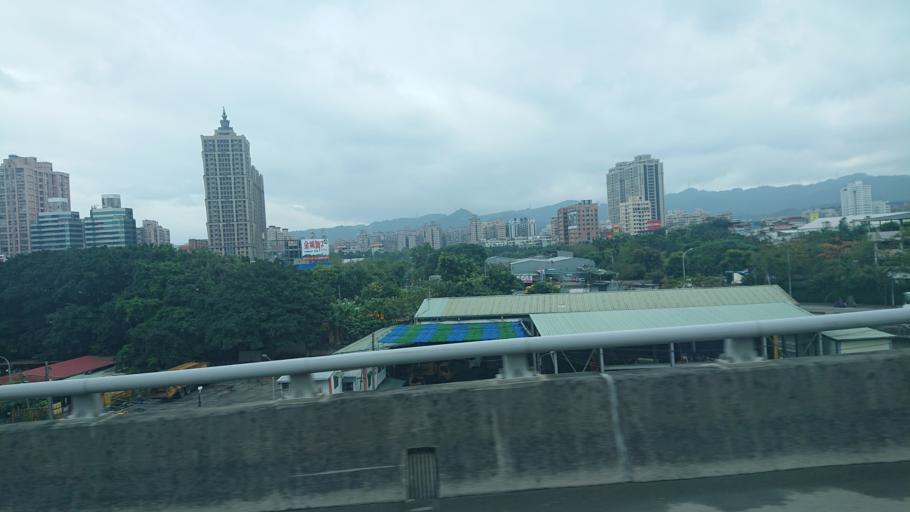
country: TW
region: Taipei
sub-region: Taipei
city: Banqiao
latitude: 24.9948
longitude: 121.4466
